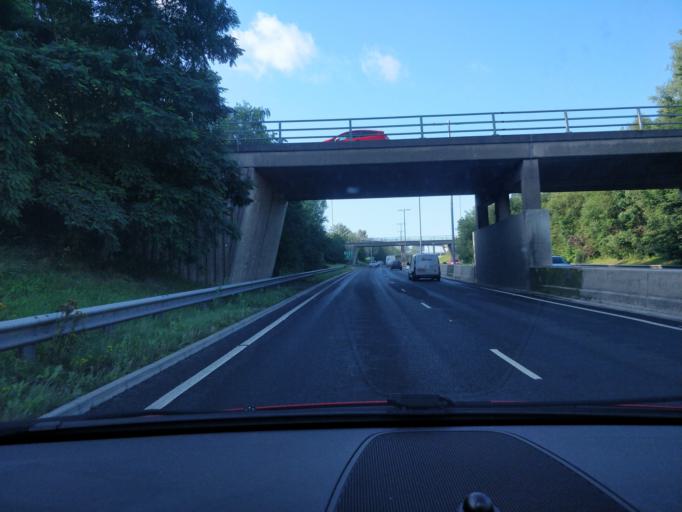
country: GB
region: England
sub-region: Borough of Halton
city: Halton
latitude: 53.3303
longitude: -2.7036
